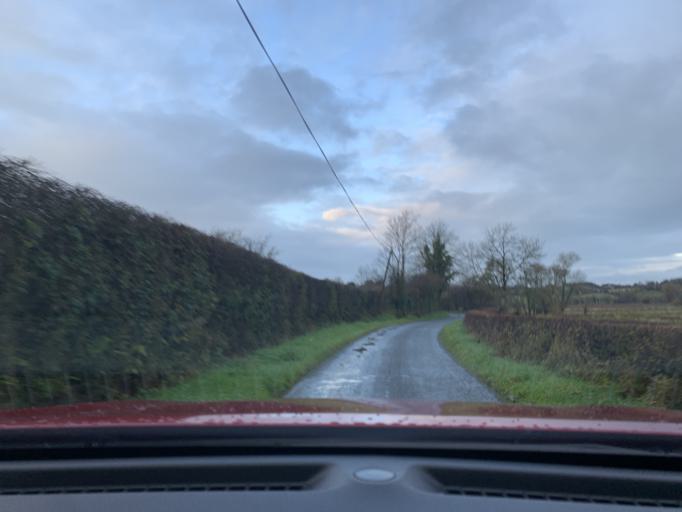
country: IE
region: Connaught
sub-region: Sligo
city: Ballymote
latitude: 54.0470
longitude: -8.5400
